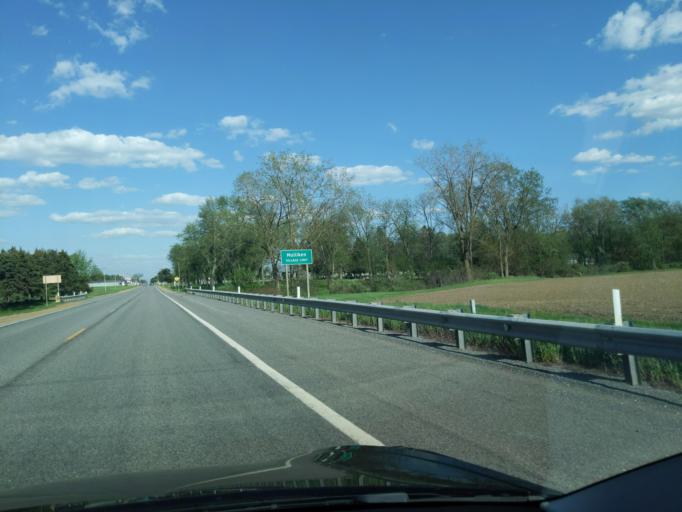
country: US
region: Michigan
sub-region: Ionia County
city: Portland
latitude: 42.7556
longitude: -84.9067
